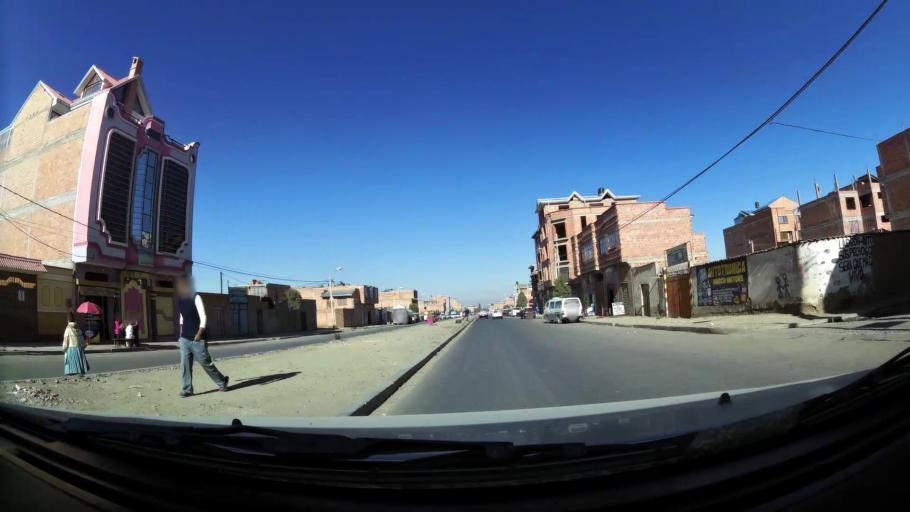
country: BO
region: La Paz
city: La Paz
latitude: -16.5433
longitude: -68.1712
